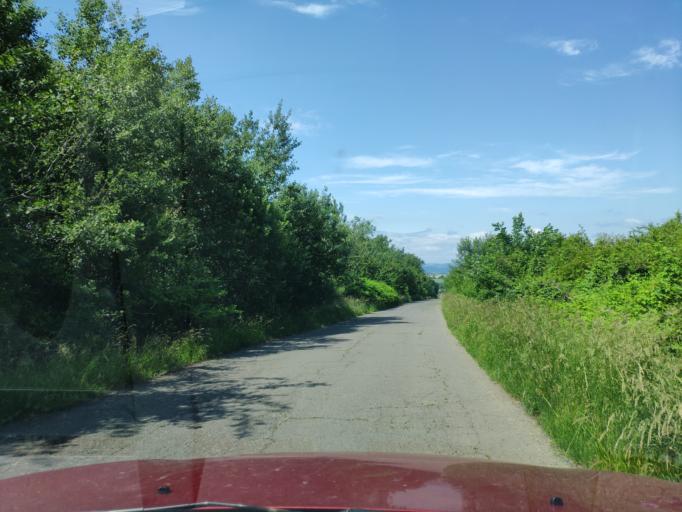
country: SK
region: Presovsky
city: Vranov nad Topl'ou
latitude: 48.8160
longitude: 21.6378
